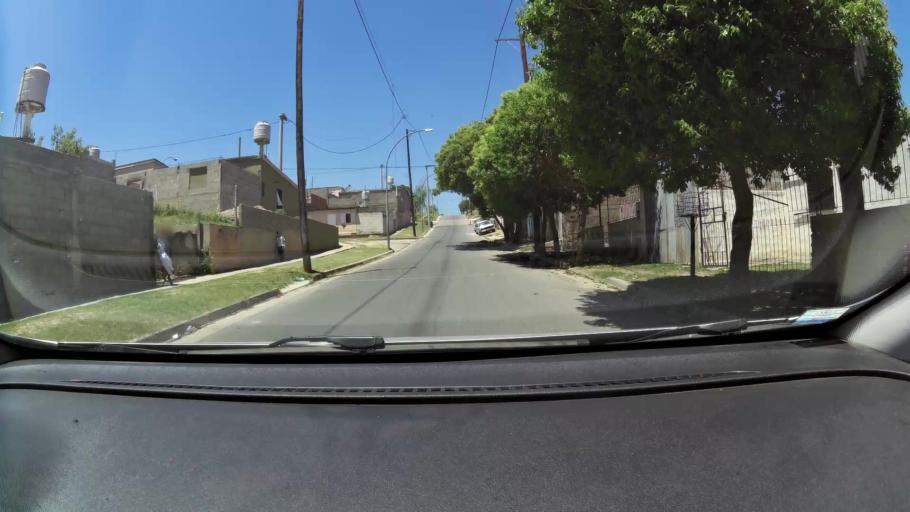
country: AR
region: Cordoba
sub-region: Departamento de Capital
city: Cordoba
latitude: -31.4200
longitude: -64.1193
